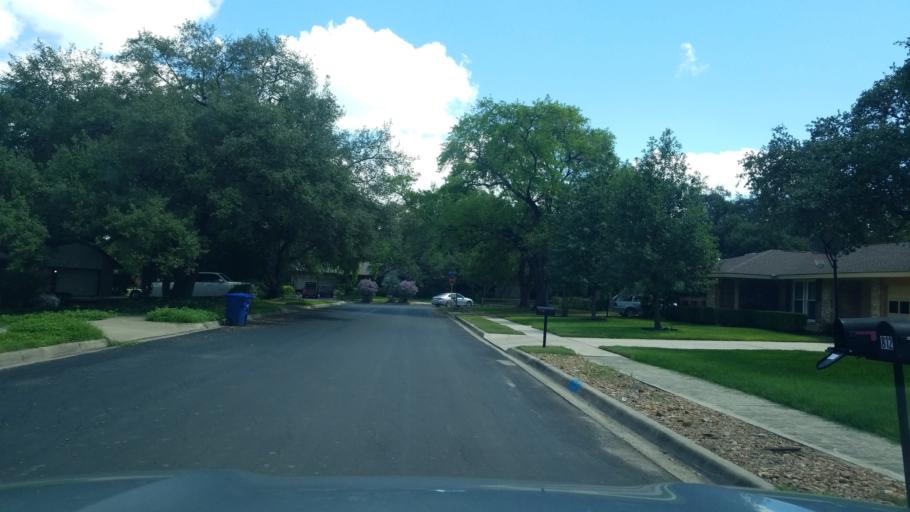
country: US
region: Texas
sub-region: Bexar County
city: Castle Hills
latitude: 29.5471
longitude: -98.5056
